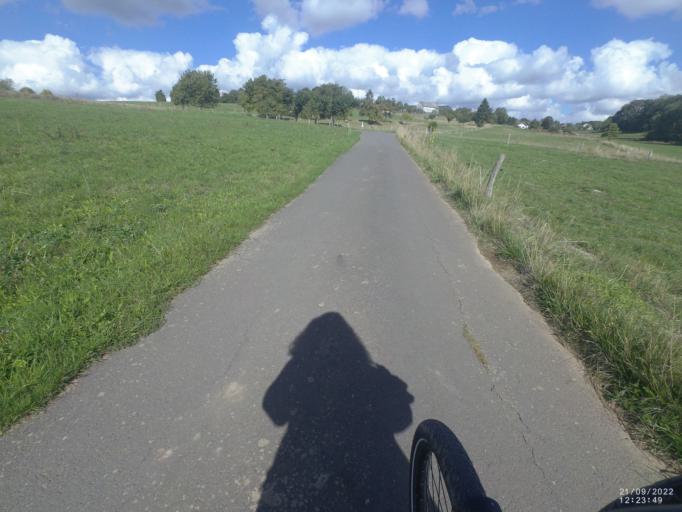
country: DE
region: Rheinland-Pfalz
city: Ellscheid
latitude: 50.1465
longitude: 6.9148
